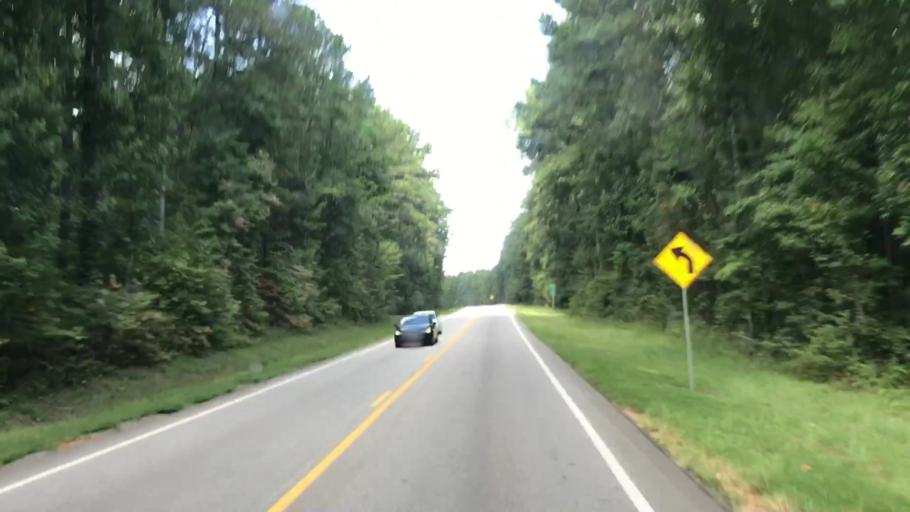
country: US
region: Georgia
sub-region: Greene County
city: Greensboro
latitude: 33.6989
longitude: -83.2805
